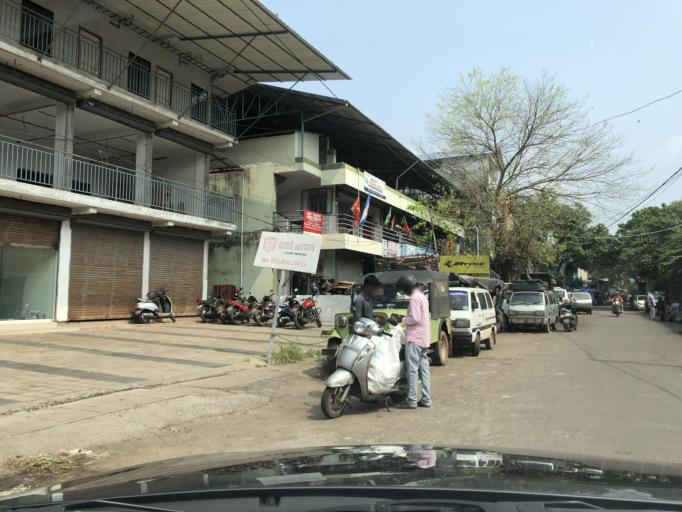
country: IN
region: Kerala
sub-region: Kozhikode
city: Kozhikode
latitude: 11.2523
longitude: 75.7773
